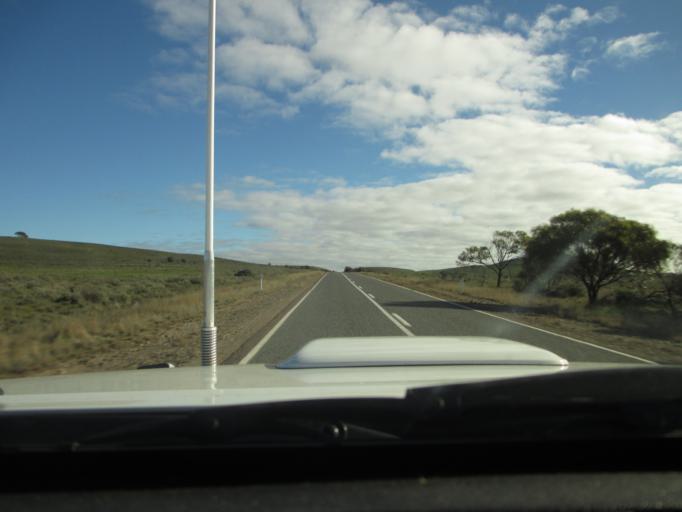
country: AU
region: South Australia
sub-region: Peterborough
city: Peterborough
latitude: -32.6173
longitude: 138.5759
